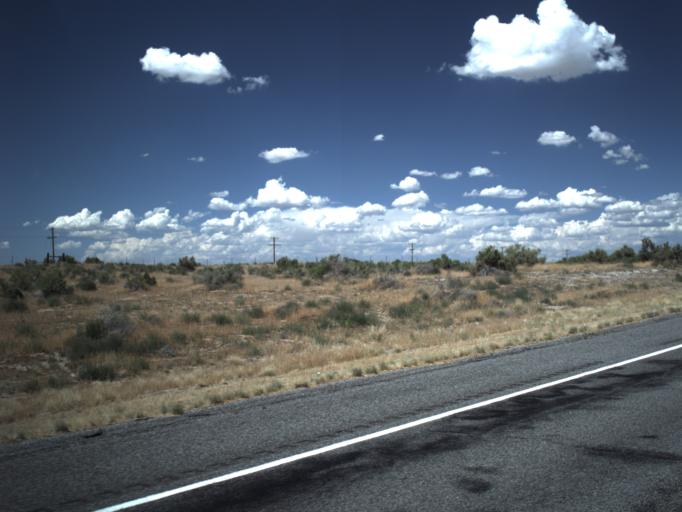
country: US
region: Utah
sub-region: Millard County
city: Delta
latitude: 39.4104
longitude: -112.4878
